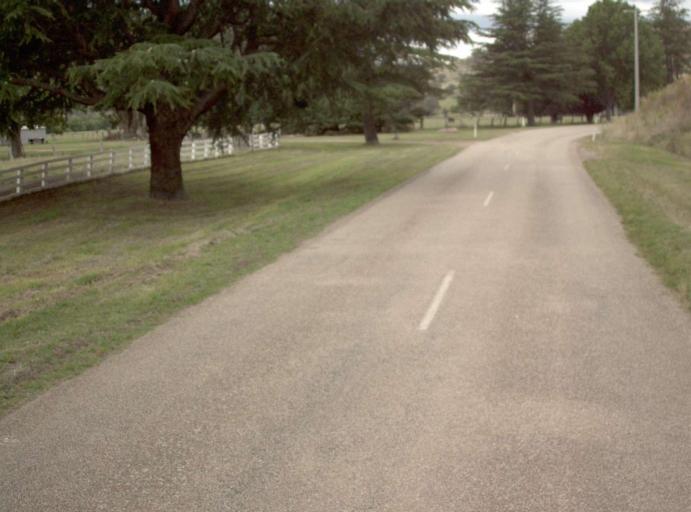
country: AU
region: Victoria
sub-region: East Gippsland
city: Bairnsdale
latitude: -37.4678
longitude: 147.2540
